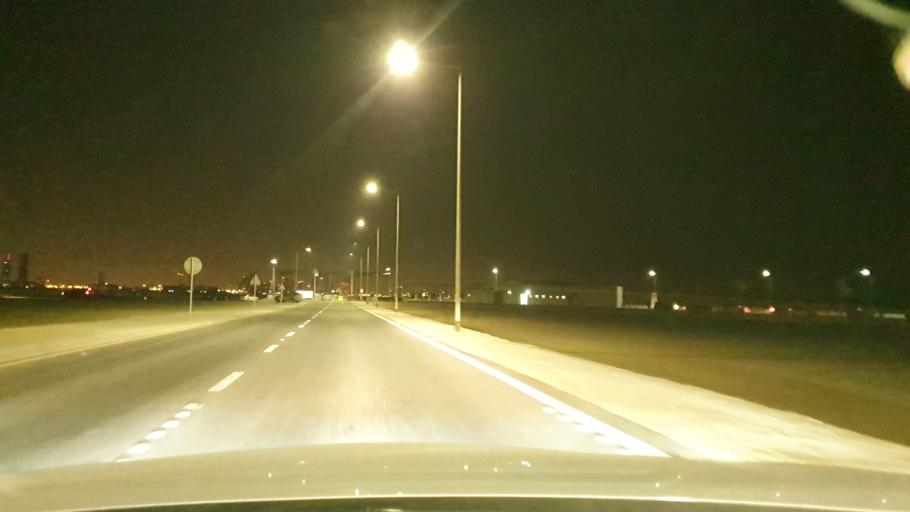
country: BH
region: Muharraq
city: Al Muharraq
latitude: 26.2850
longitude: 50.5780
